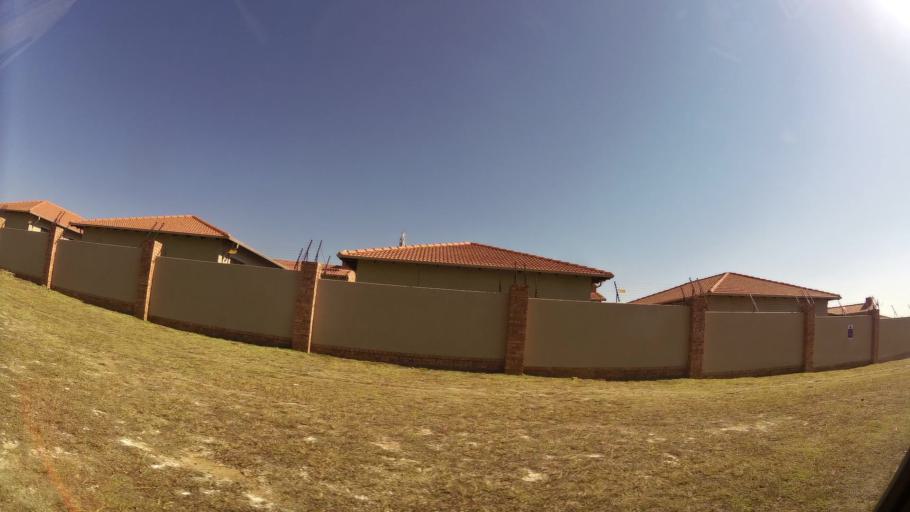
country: ZA
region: Gauteng
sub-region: City of Johannesburg Metropolitan Municipality
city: Midrand
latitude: -25.9662
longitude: 28.1159
